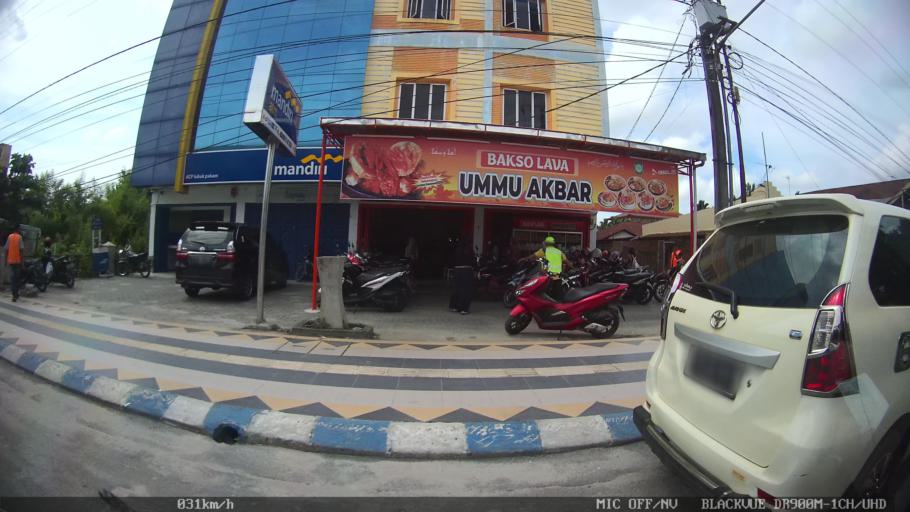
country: ID
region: North Sumatra
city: Percut
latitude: 3.5587
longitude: 98.8680
